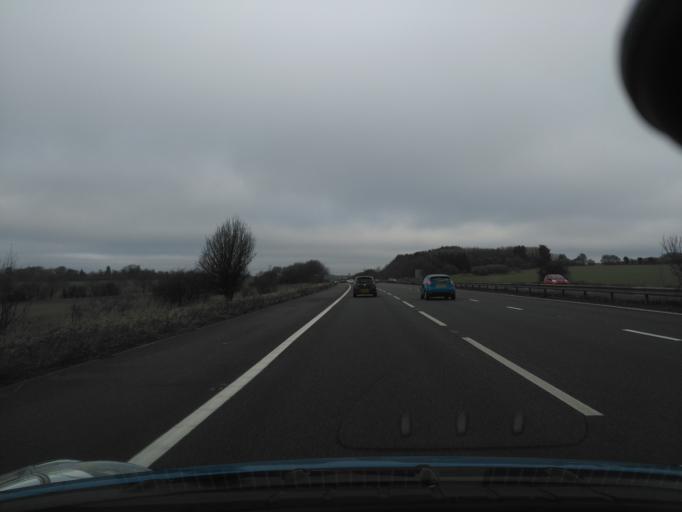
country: GB
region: England
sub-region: Hertfordshire
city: Letchworth Garden City
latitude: 51.9447
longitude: -0.2125
